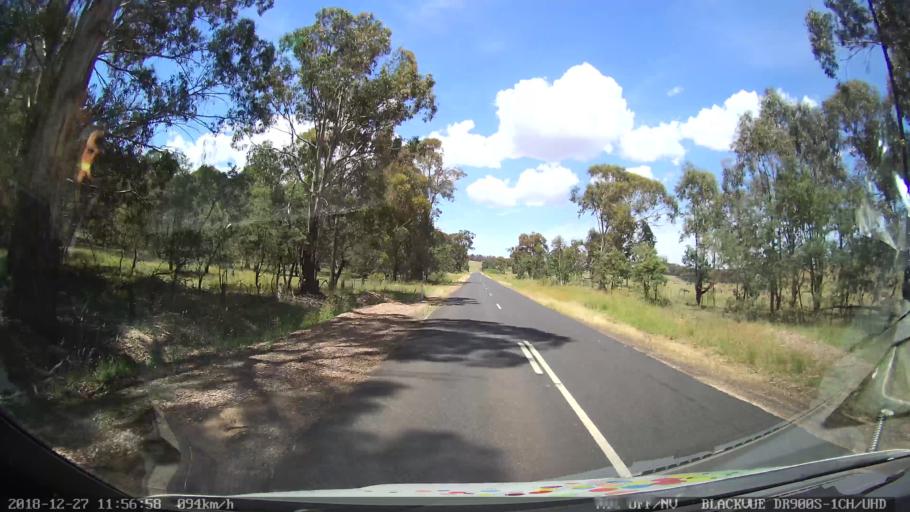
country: AU
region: New South Wales
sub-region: Blayney
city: Blayney
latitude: -33.7050
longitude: 149.3874
